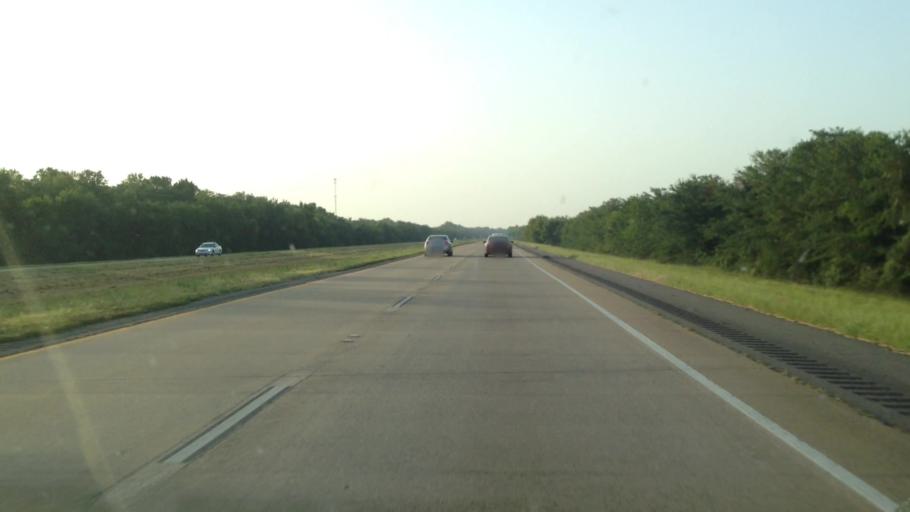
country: US
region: Louisiana
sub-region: Natchitoches Parish
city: Vienna Bend
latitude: 31.5592
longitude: -92.9807
